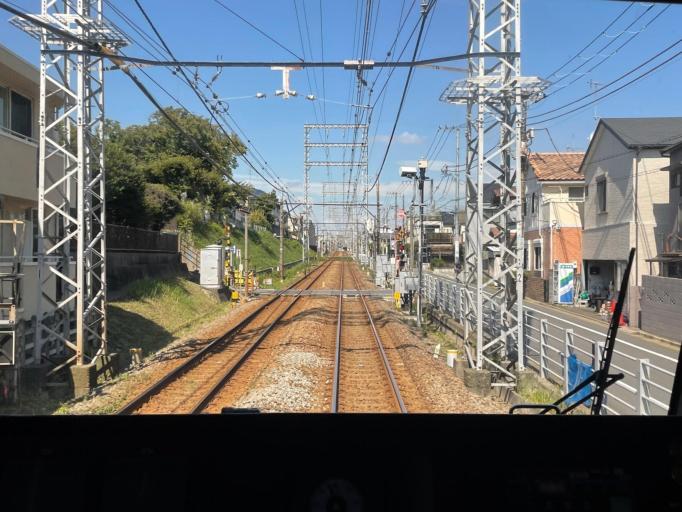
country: JP
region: Kanagawa
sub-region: Kawasaki-shi
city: Kawasaki
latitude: 35.5741
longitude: 139.6906
